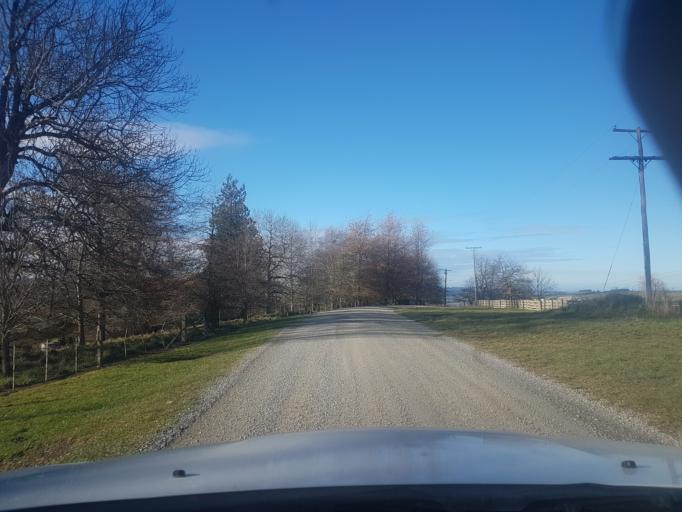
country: NZ
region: Canterbury
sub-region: Timaru District
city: Pleasant Point
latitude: -44.1694
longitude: 170.9246
